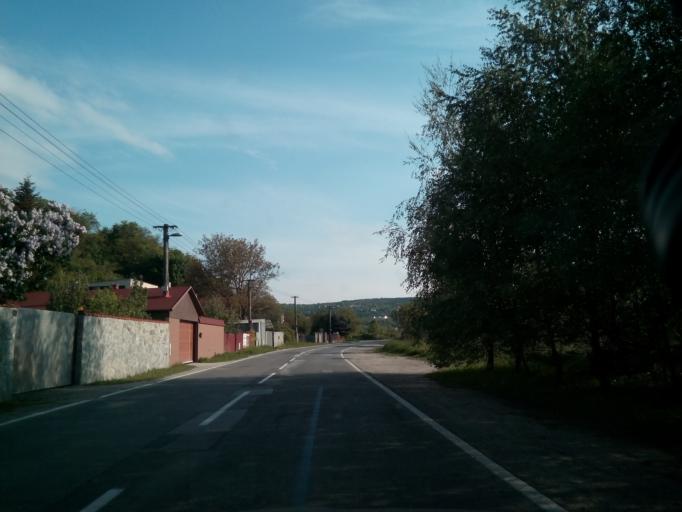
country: SK
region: Kosicky
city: Kosice
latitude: 48.7494
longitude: 21.2486
